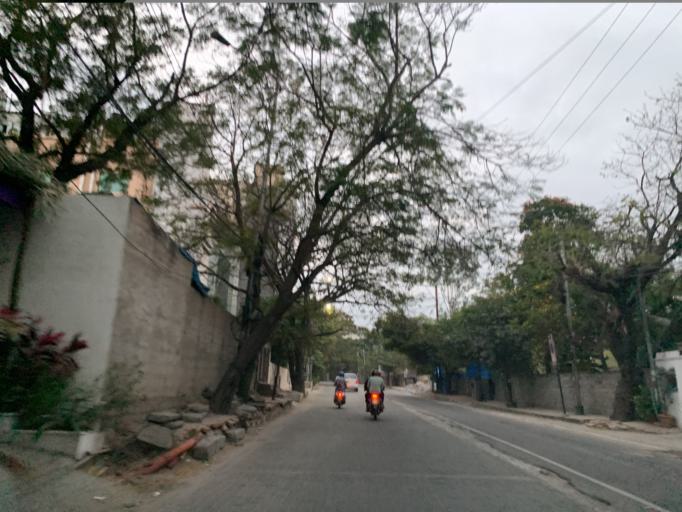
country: IN
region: Telangana
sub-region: Rangareddi
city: Kukatpalli
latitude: 17.4353
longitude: 78.3980
